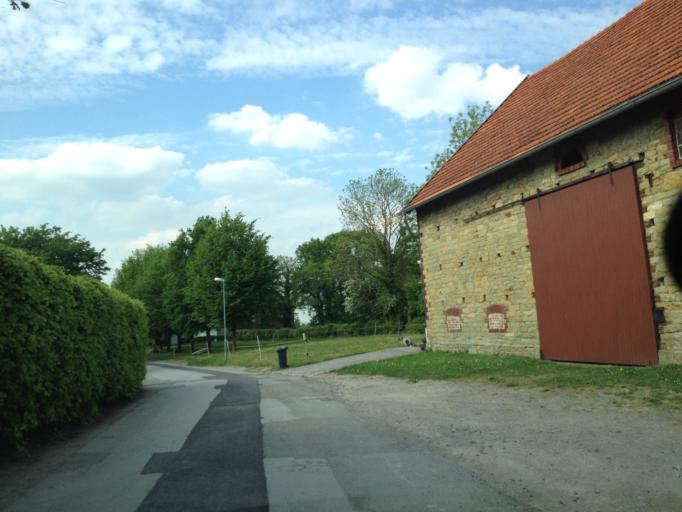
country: DE
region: North Rhine-Westphalia
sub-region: Regierungsbezirk Arnsberg
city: Soest
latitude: 51.5390
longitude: 8.0279
